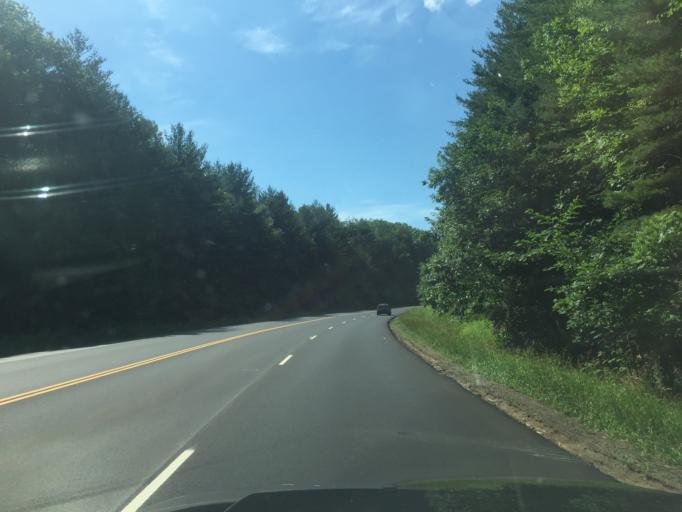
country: US
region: Connecticut
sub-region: Litchfield County
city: Winsted
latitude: 41.9319
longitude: -73.0860
